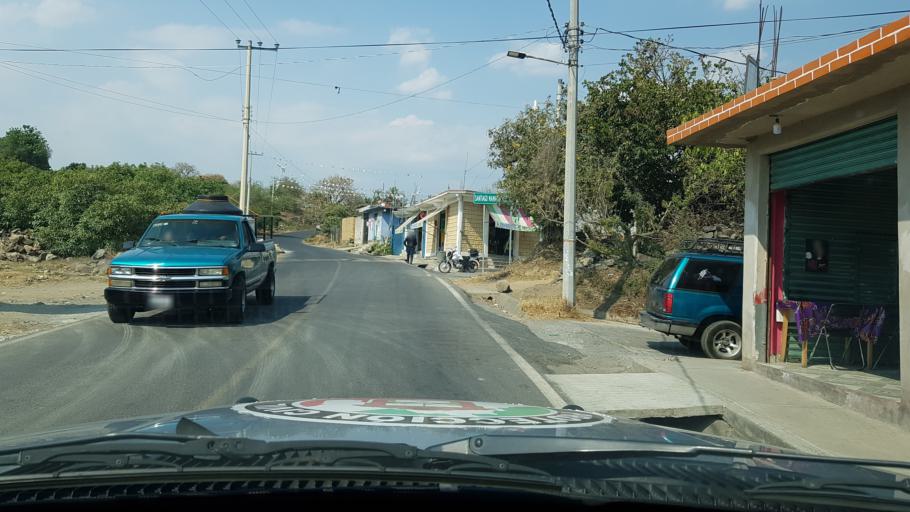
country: MX
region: Mexico
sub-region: Atlautla
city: San Andres Tlalamac
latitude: 18.9704
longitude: -98.8171
